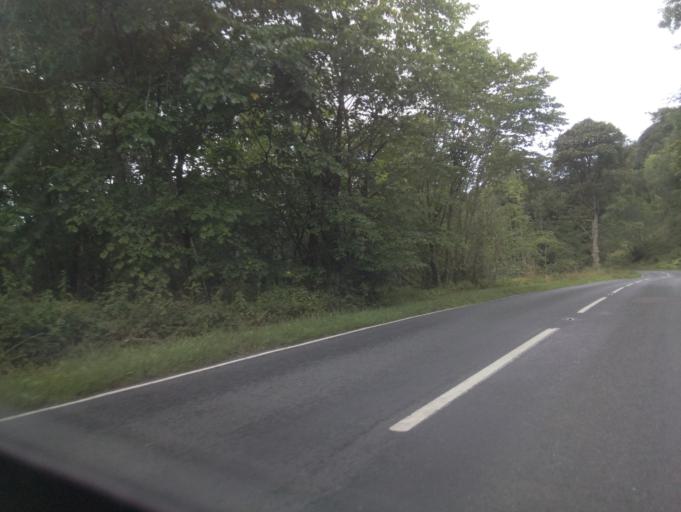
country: GB
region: England
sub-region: North Yorkshire
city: Leyburn
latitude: 54.3981
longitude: -1.8253
